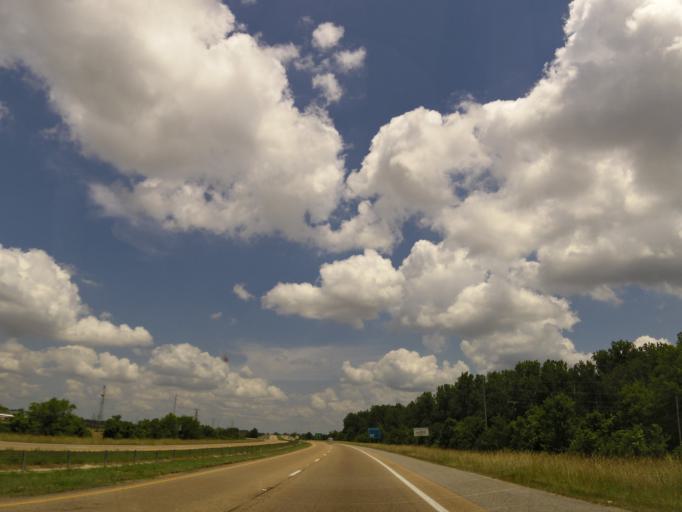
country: US
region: Mississippi
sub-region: Lee County
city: Tupelo
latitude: 34.2483
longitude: -88.6941
